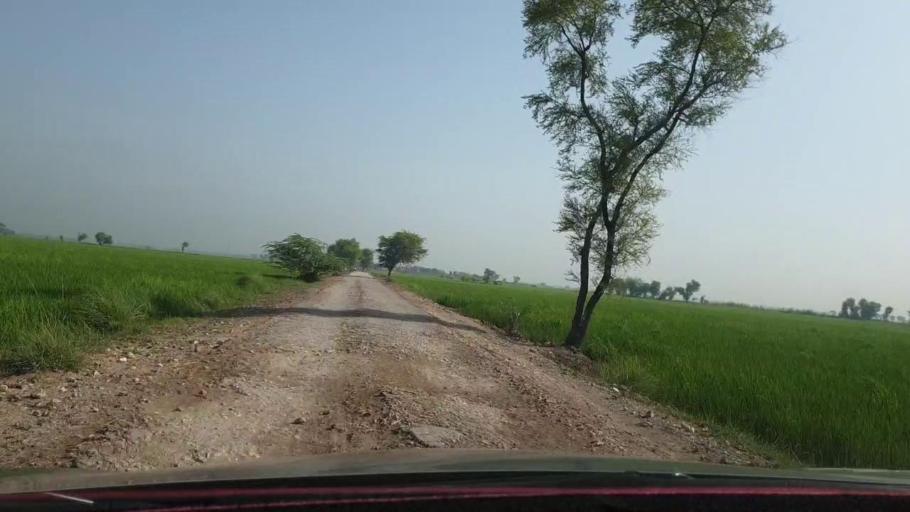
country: PK
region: Sindh
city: Nasirabad
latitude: 27.4689
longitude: 67.9221
